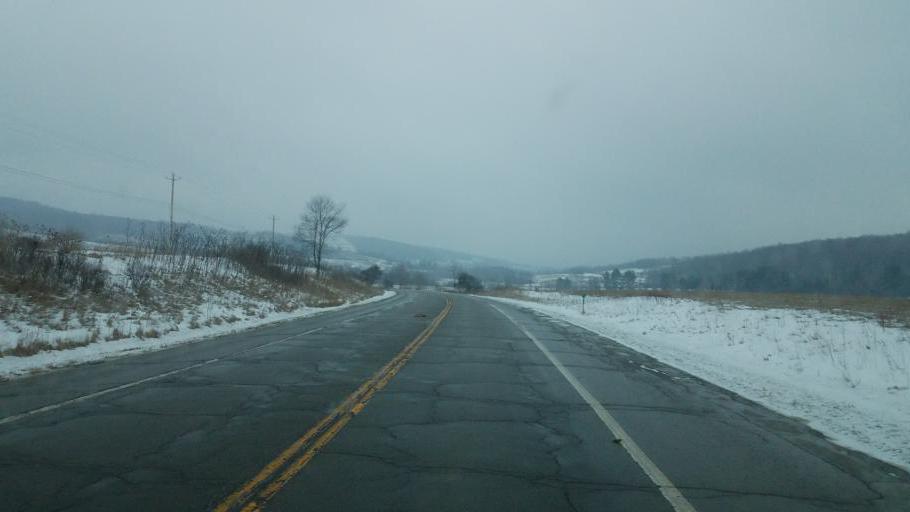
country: US
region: Pennsylvania
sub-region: Tioga County
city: Elkland
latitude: 42.0978
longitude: -77.4425
